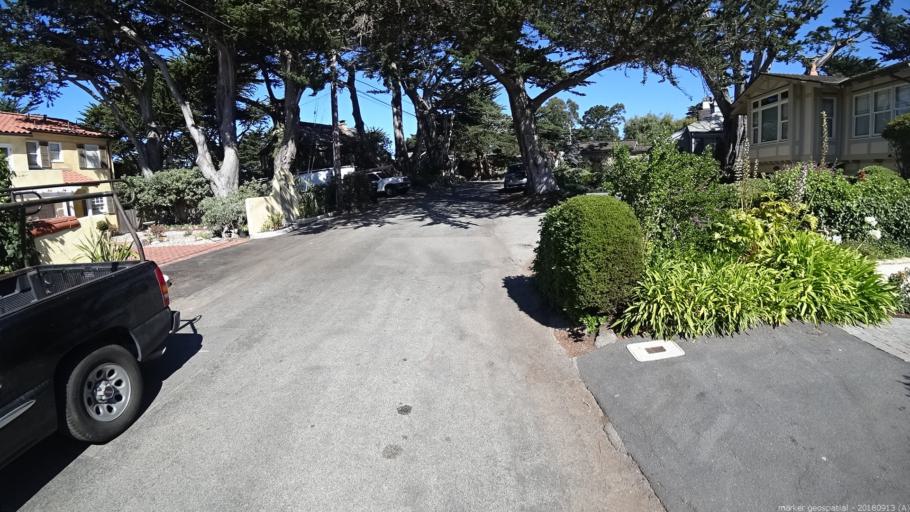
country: US
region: California
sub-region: Monterey County
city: Carmel-by-the-Sea
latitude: 36.5404
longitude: -121.9318
